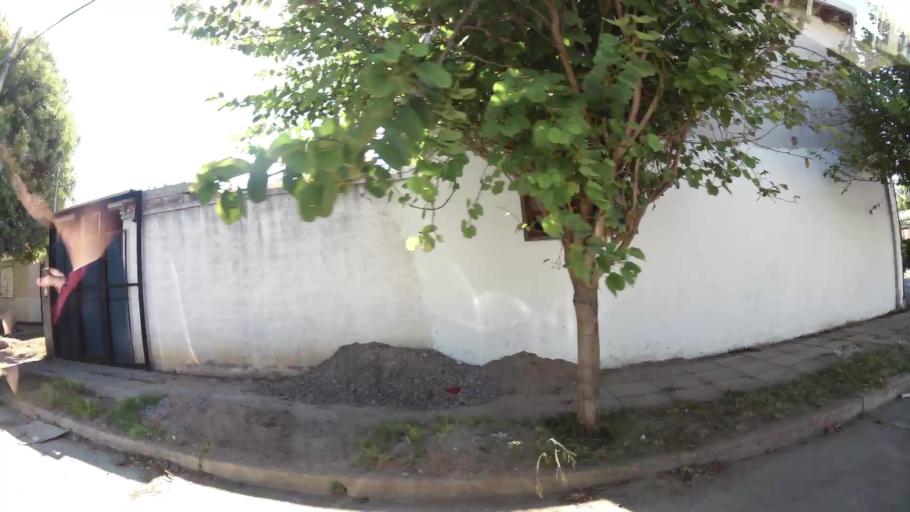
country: AR
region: Cordoba
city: Villa Allende
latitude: -31.3407
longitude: -64.2392
